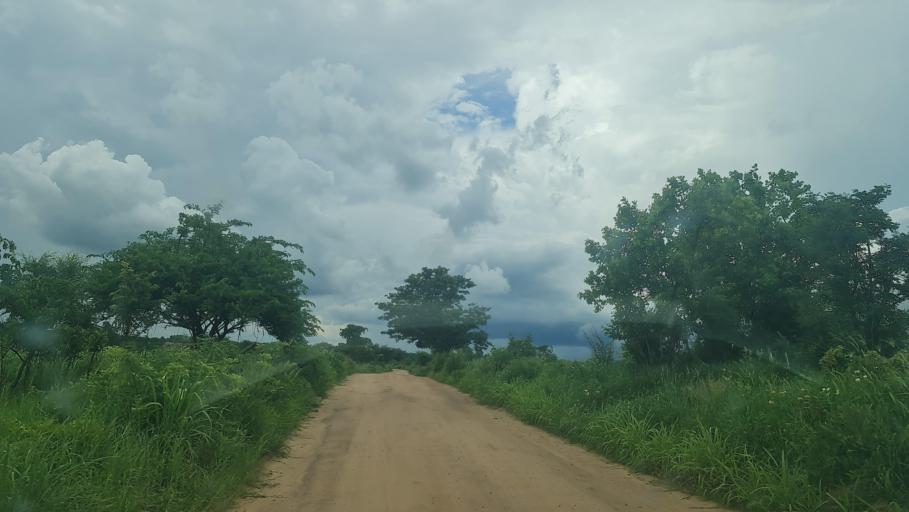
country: MW
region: Southern Region
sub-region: Nsanje District
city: Nsanje
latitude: -17.5711
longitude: 35.6525
